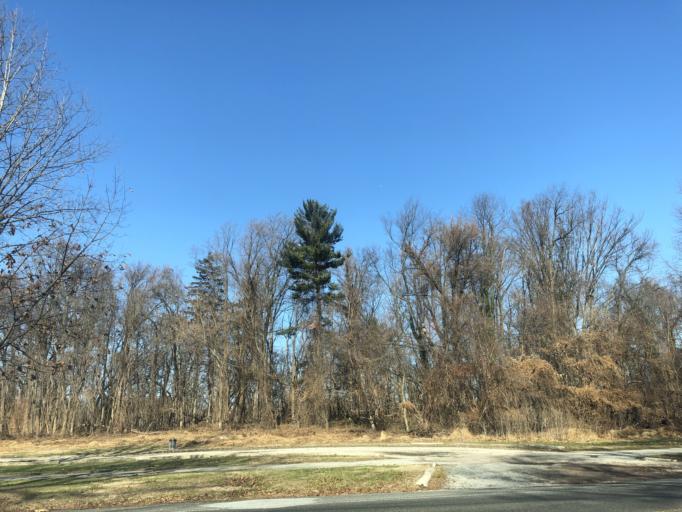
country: US
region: Pennsylvania
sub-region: Montgomery County
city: Bala-Cynwyd
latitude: 39.9944
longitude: -75.2120
